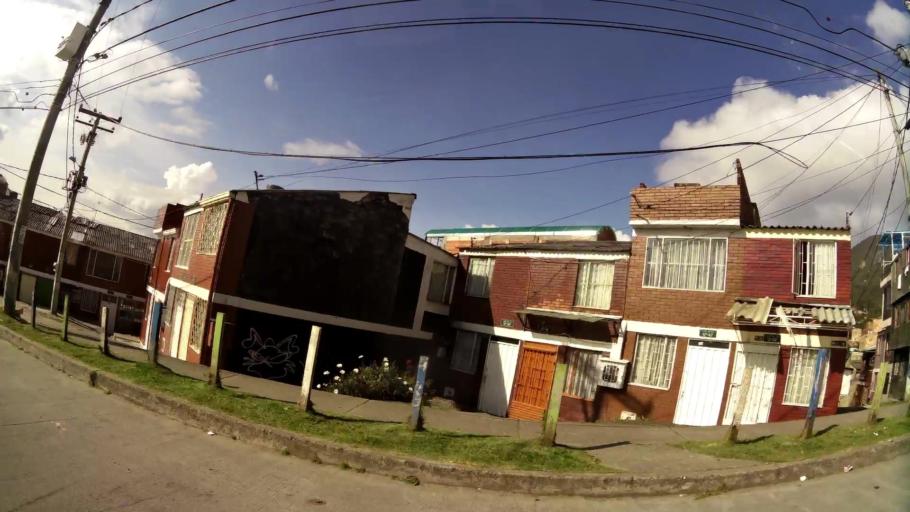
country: CO
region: Bogota D.C.
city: Bogota
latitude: 4.5390
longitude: -74.0871
